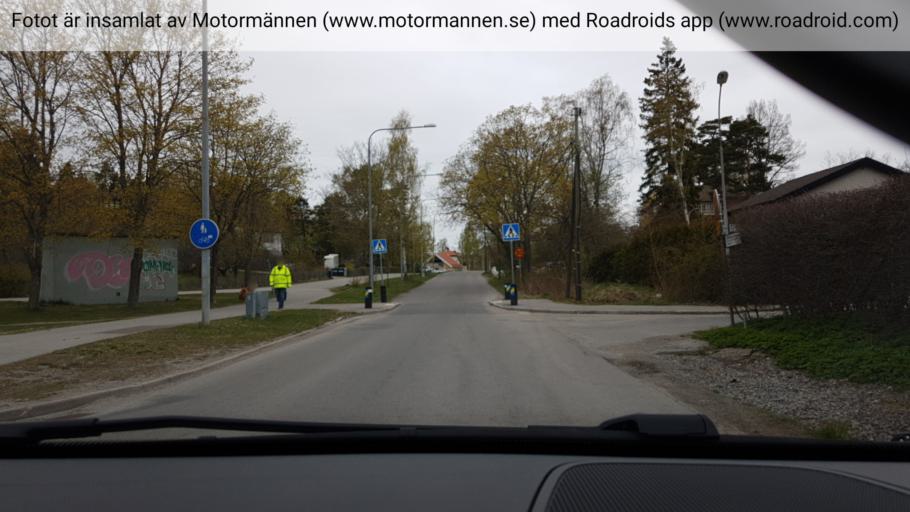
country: SE
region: Stockholm
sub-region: Huddinge Kommun
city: Huddinge
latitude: 59.2368
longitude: 17.9952
